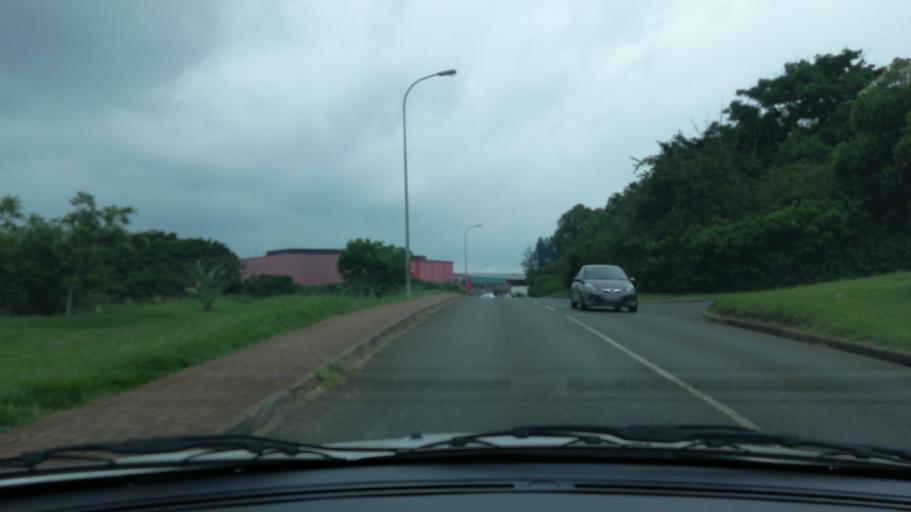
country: ZA
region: KwaZulu-Natal
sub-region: uThungulu District Municipality
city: Empangeni
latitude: -28.7466
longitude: 31.8851
